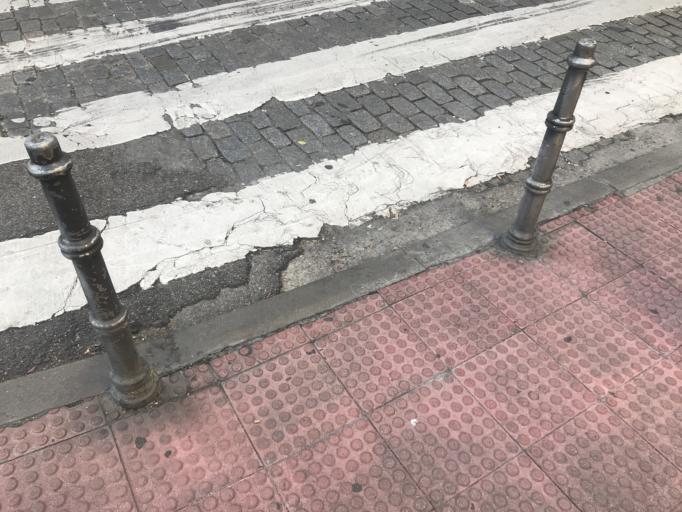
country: ES
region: Madrid
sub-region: Provincia de Madrid
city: Chamberi
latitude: 40.4288
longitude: -3.7078
